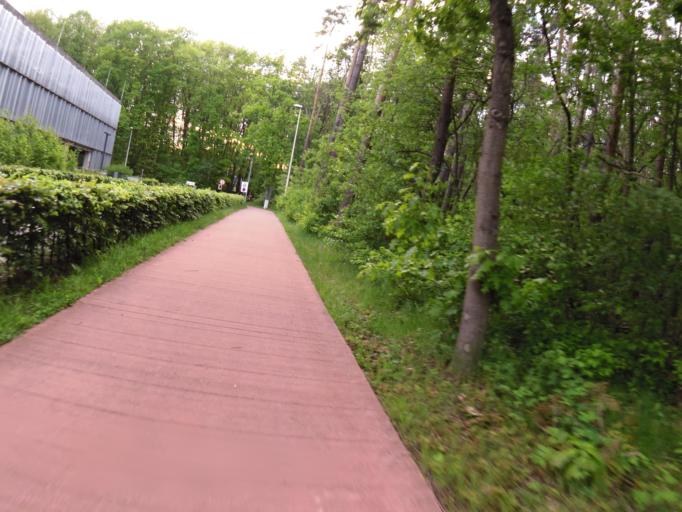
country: BE
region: Flanders
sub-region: Provincie Limburg
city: Genk
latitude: 50.9594
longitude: 5.5169
